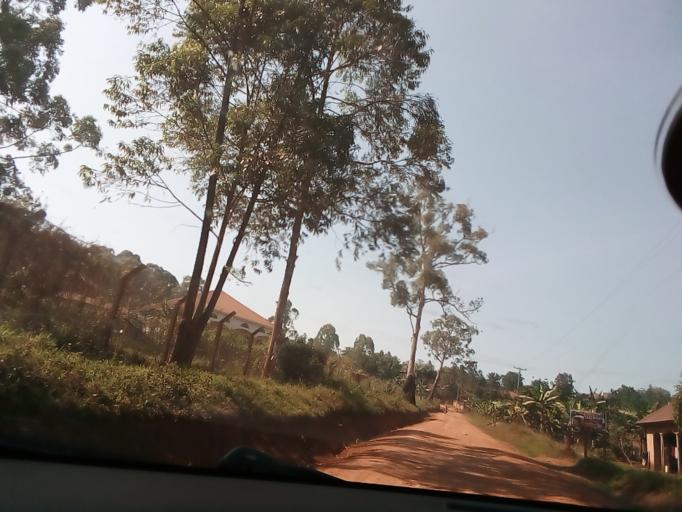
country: UG
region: Central Region
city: Masaka
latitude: -0.3306
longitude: 31.7336
